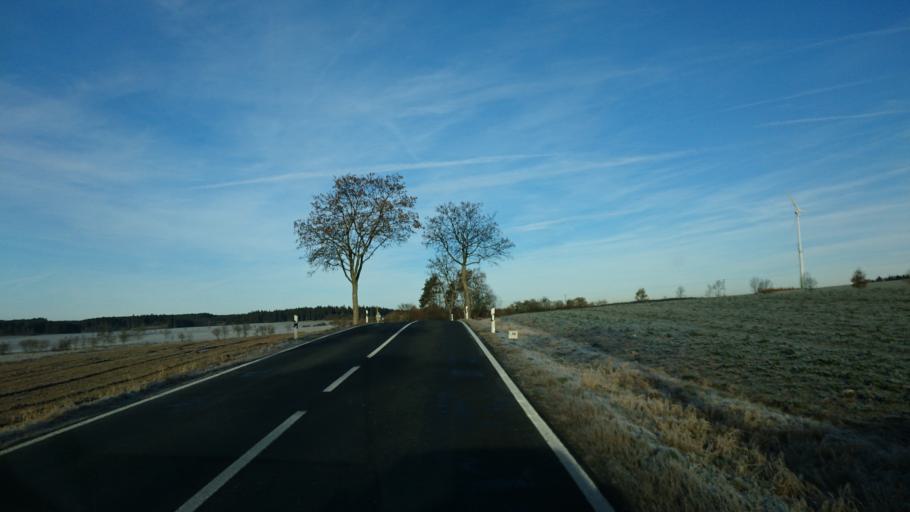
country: DE
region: Thuringia
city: Tanna
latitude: 50.5292
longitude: 11.8752
